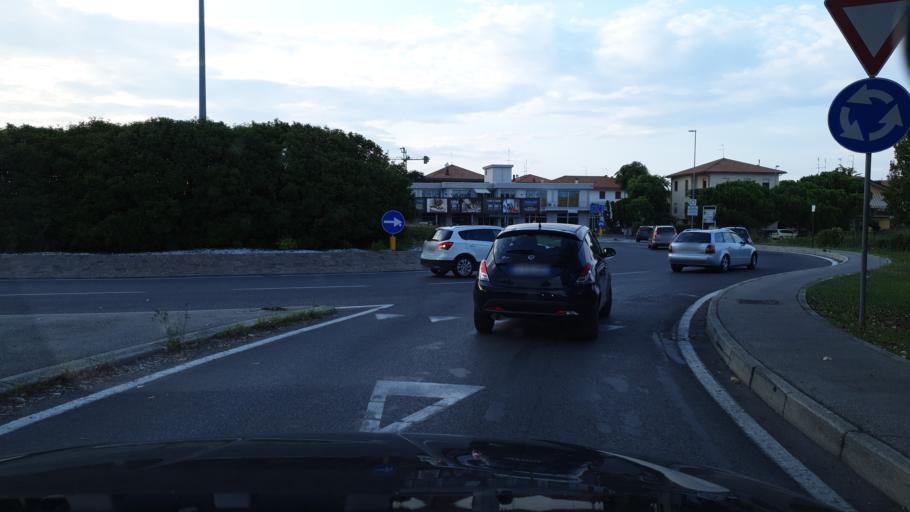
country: IT
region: Emilia-Romagna
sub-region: Provincia di Rimini
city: Rivazzurra
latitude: 44.0369
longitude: 12.5982
